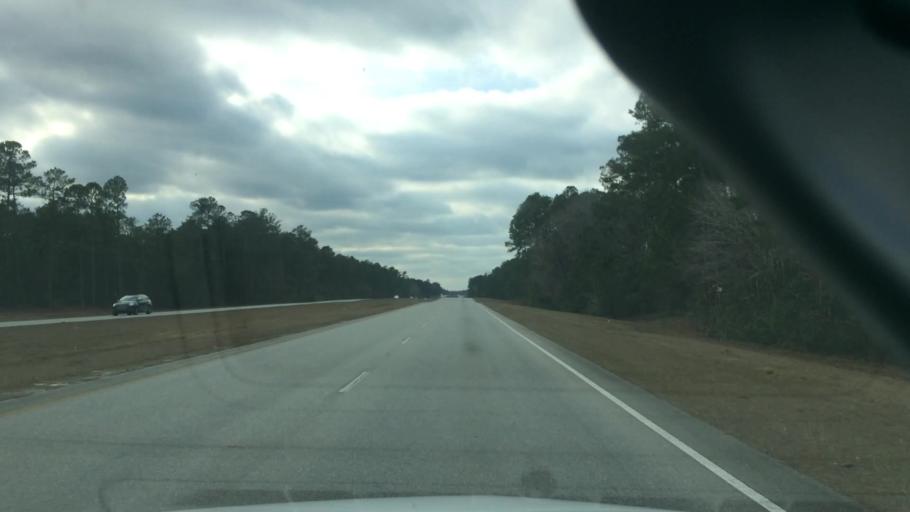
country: US
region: North Carolina
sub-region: Brunswick County
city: Bolivia
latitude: 34.0488
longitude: -78.2235
